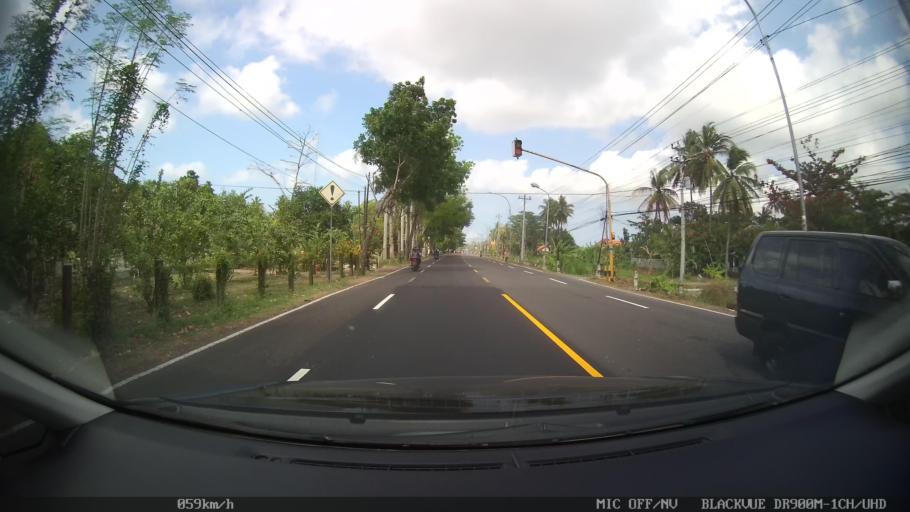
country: ID
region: Daerah Istimewa Yogyakarta
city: Srandakan
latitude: -7.8738
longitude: 110.1371
